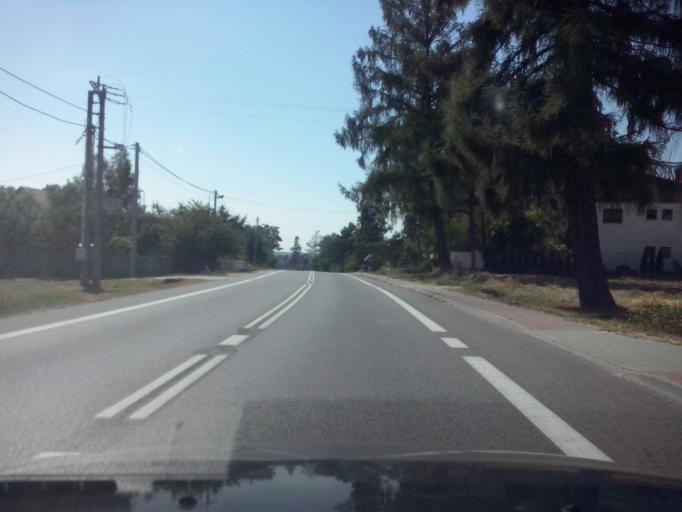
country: PL
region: Swietokrzyskie
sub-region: Powiat kielecki
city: Wola Jachowa
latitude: 50.8518
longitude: 20.8802
